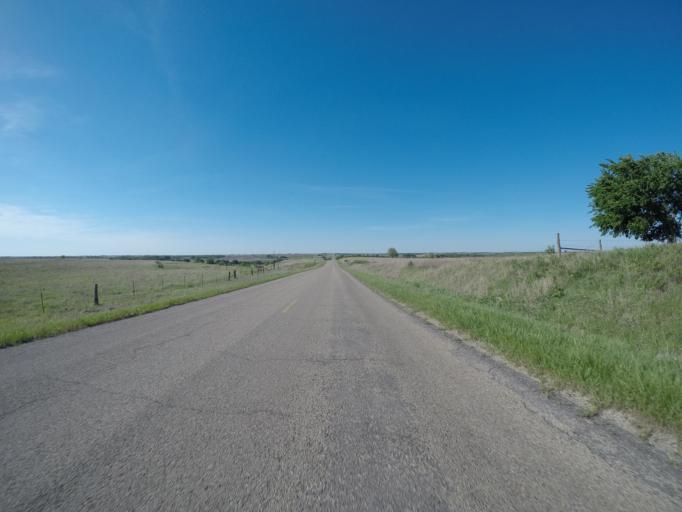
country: US
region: Kansas
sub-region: Clay County
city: Clay Center
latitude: 39.4993
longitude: -96.9967
